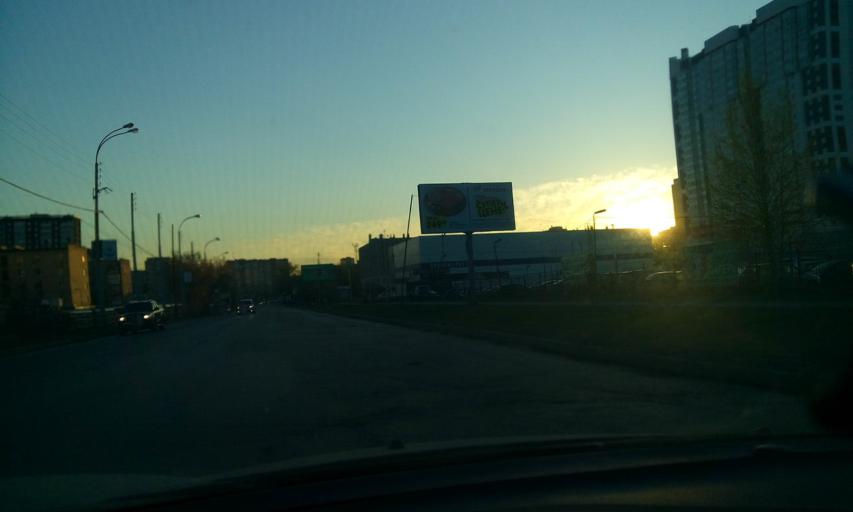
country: RU
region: Sverdlovsk
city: Yekaterinburg
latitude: 56.8350
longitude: 60.6940
